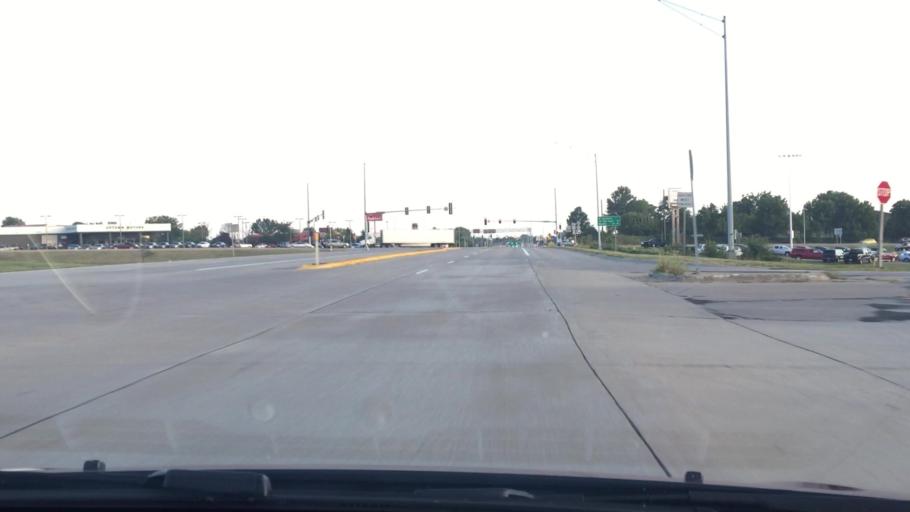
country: US
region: Iowa
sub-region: Muscatine County
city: Muscatine
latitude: 41.4554
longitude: -91.0302
